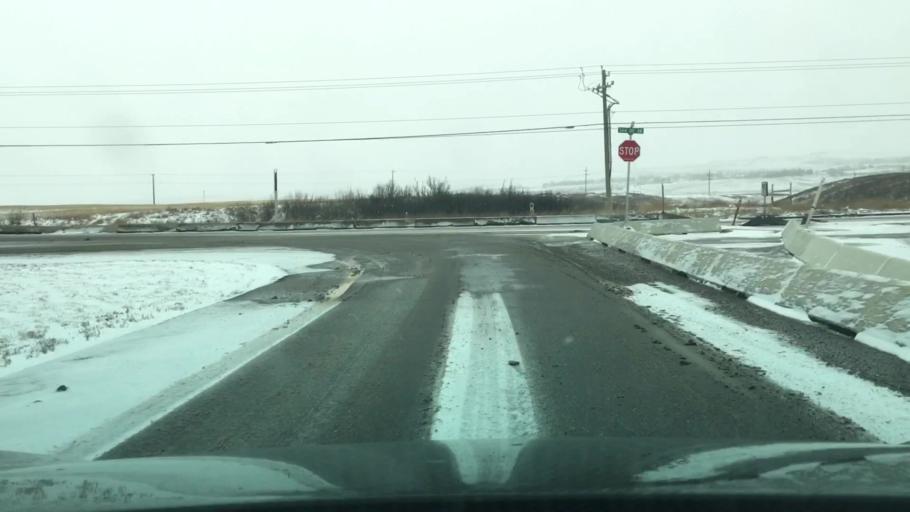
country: CA
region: Alberta
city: Calgary
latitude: 51.1828
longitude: -114.1610
